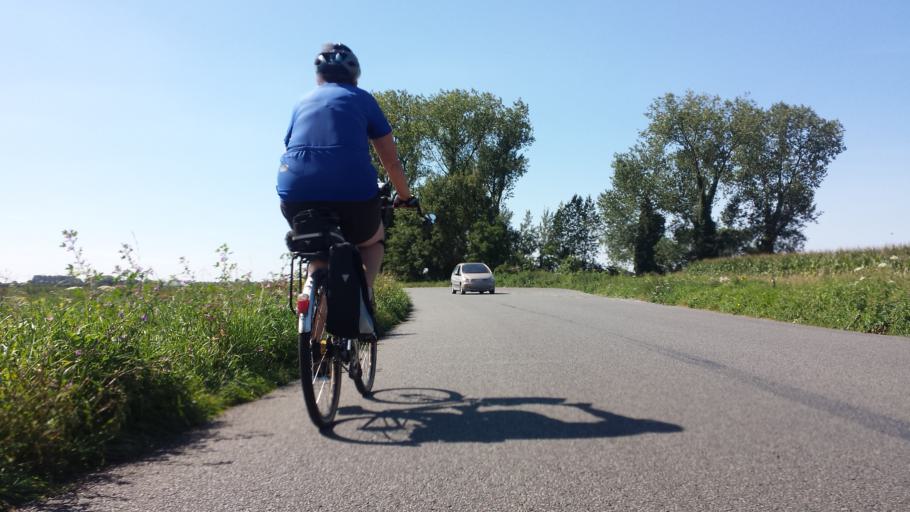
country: GB
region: England
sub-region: Cambridgeshire
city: Isleham
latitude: 52.3451
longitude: 0.3758
